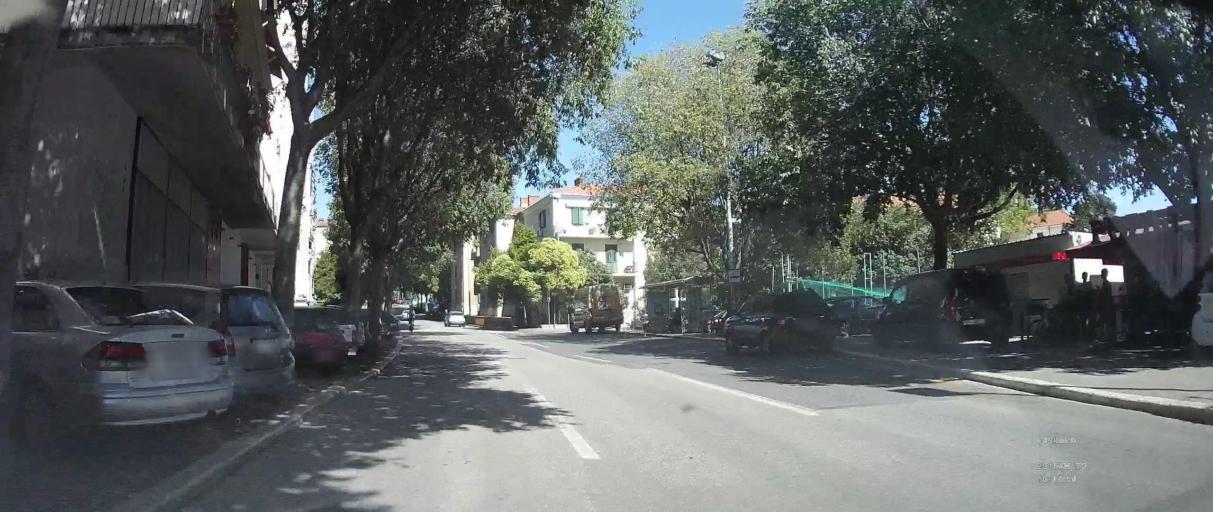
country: HR
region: Splitsko-Dalmatinska
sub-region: Grad Split
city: Split
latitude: 43.5050
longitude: 16.4495
